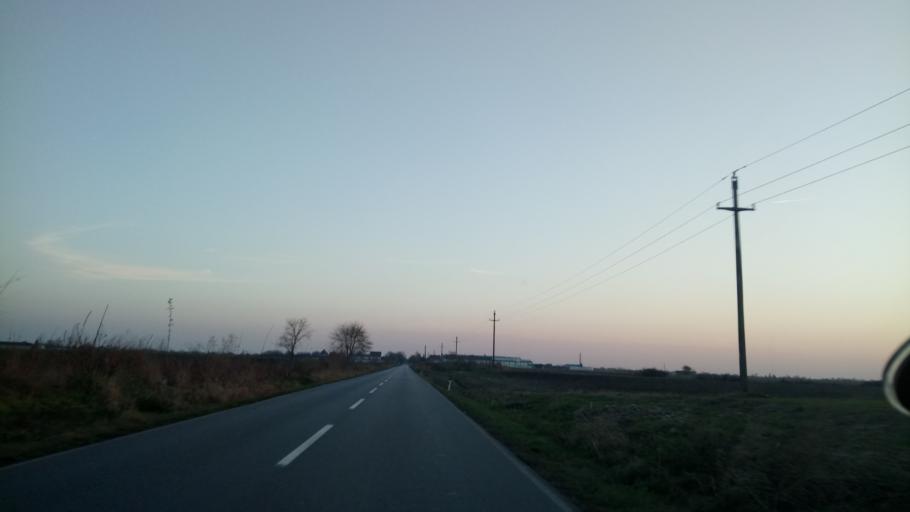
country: RS
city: Belegis
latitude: 45.0341
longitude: 20.3341
